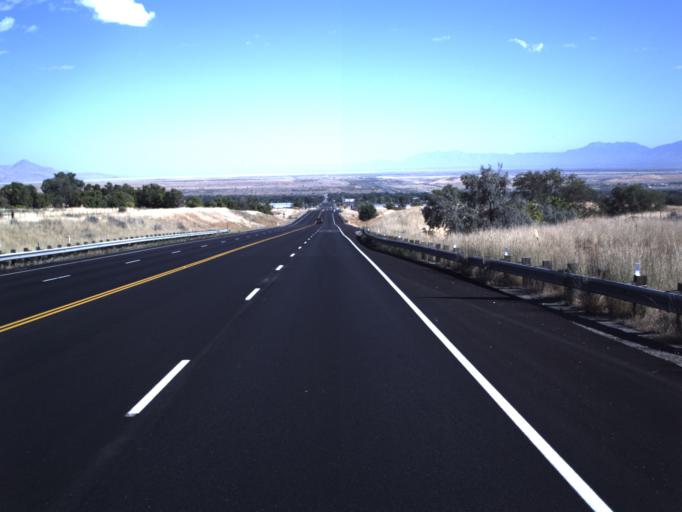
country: US
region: Utah
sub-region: Salt Lake County
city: Magna
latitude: 40.6744
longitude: -112.0919
